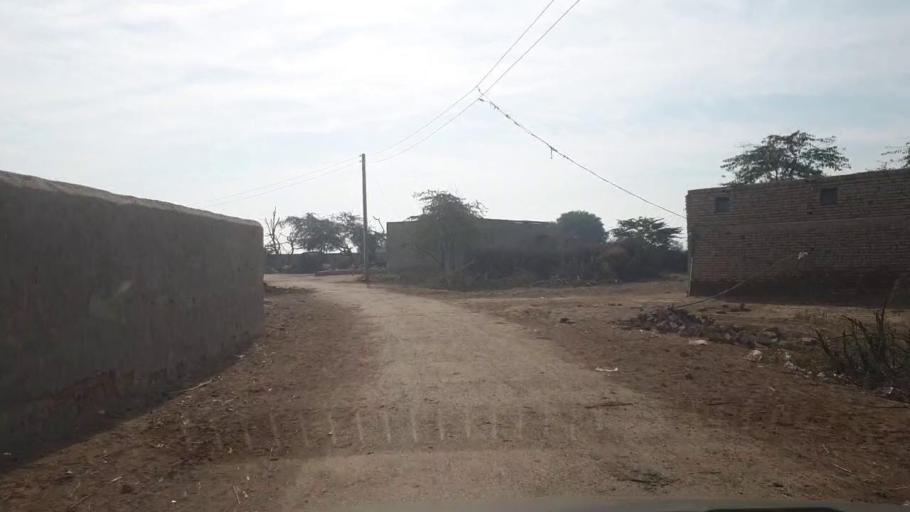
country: PK
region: Sindh
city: Shahpur Chakar
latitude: 26.1783
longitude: 68.5967
